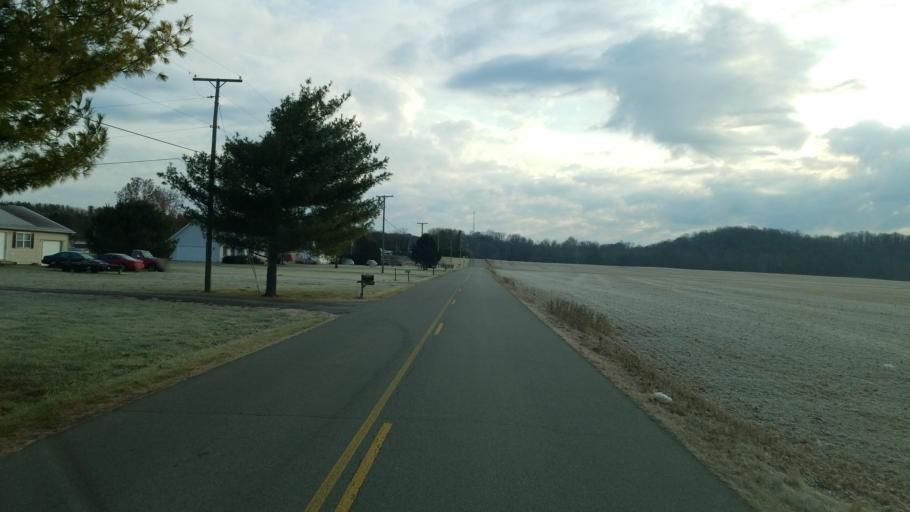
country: US
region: Ohio
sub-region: Ross County
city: Chillicothe
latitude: 39.2520
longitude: -82.8671
